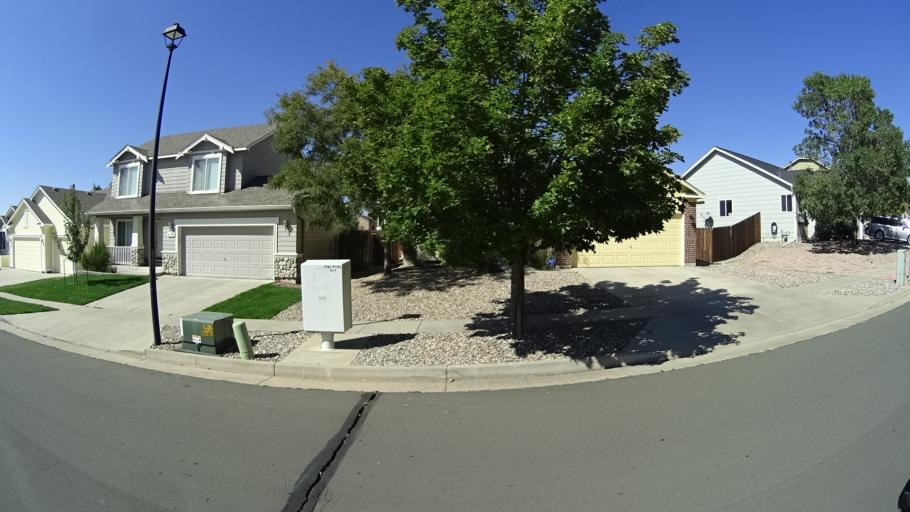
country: US
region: Colorado
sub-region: El Paso County
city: Cimarron Hills
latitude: 38.8943
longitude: -104.6910
